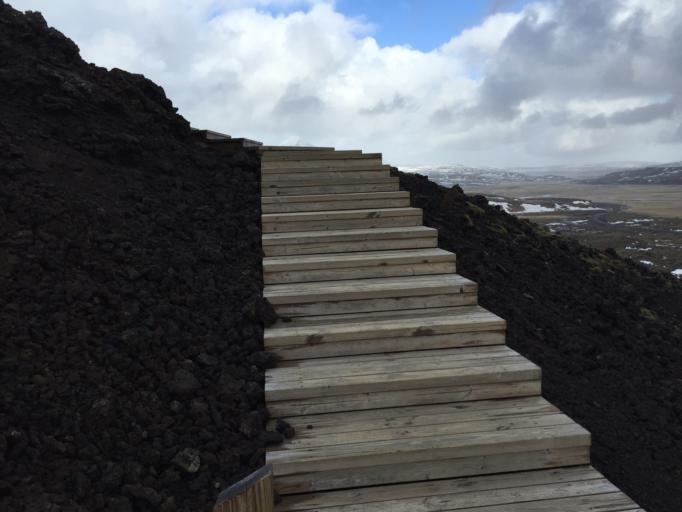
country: IS
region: West
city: Borgarnes
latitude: 64.7717
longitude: -21.5381
